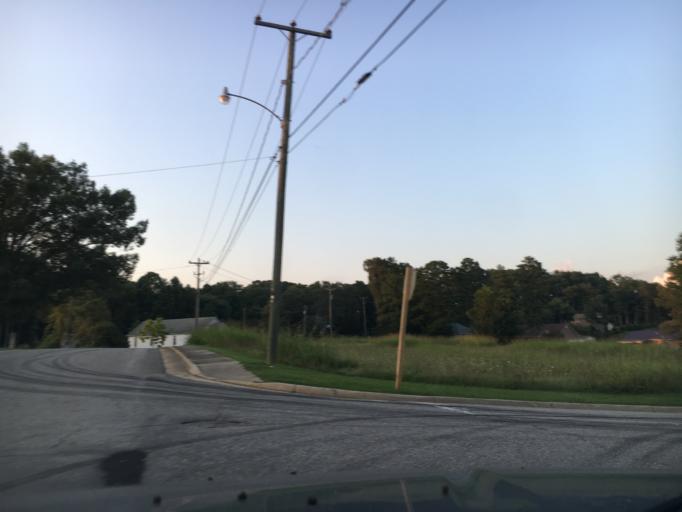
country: US
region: Virginia
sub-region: Halifax County
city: South Boston
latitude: 36.7092
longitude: -78.9073
